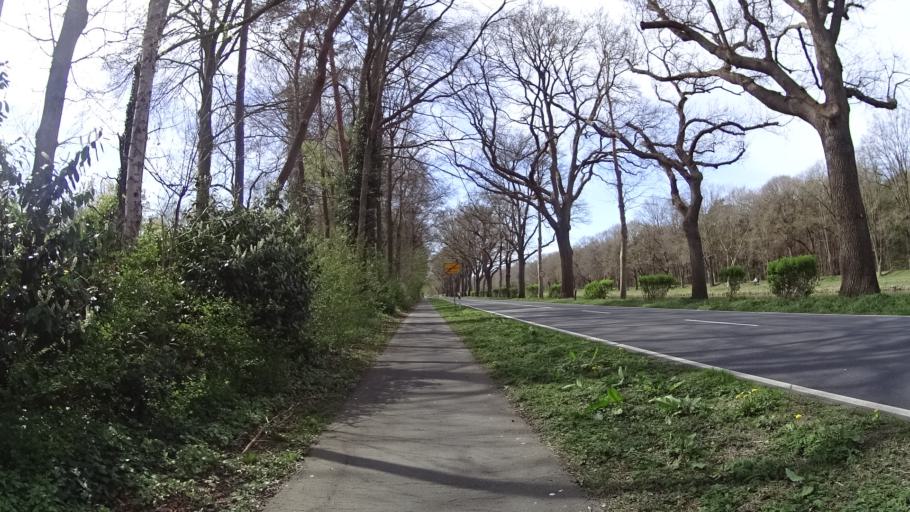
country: DE
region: Lower Saxony
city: Lingen
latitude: 52.5006
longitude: 7.3033
